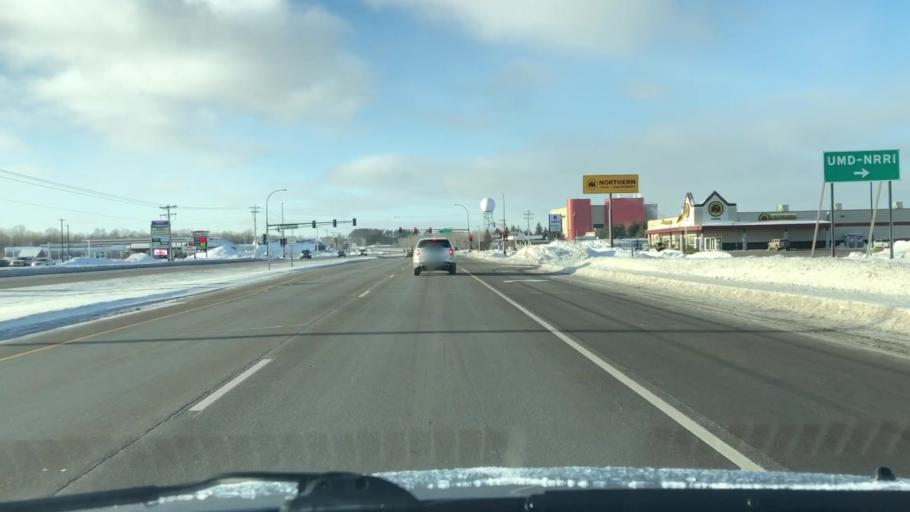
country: US
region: Minnesota
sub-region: Saint Louis County
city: Hermantown
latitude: 46.8326
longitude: -92.2037
